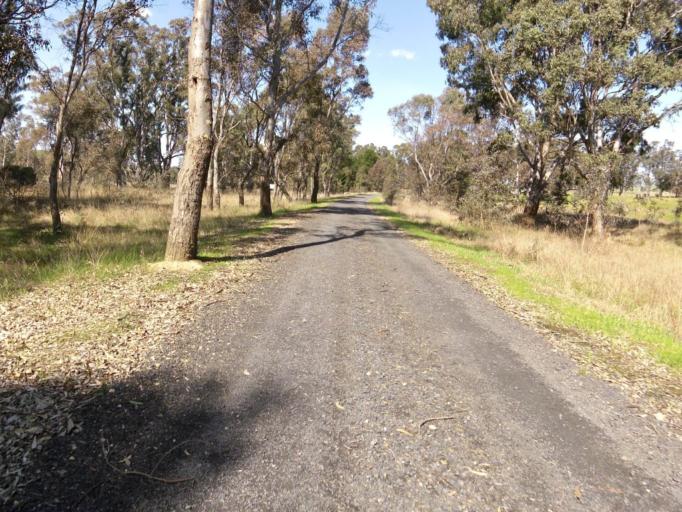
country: AU
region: Victoria
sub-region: Murrindindi
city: Alexandra
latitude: -36.9883
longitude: 145.7347
